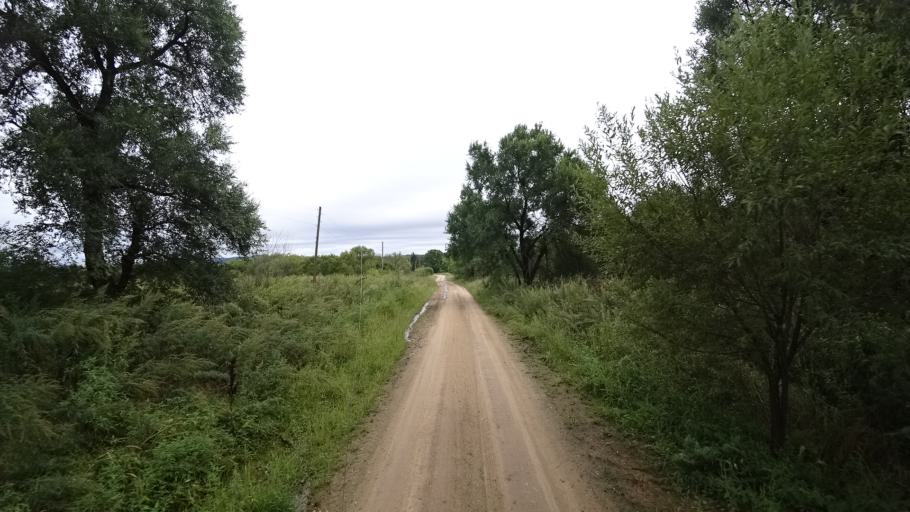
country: RU
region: Primorskiy
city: Rettikhovka
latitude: 44.1309
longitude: 132.6347
